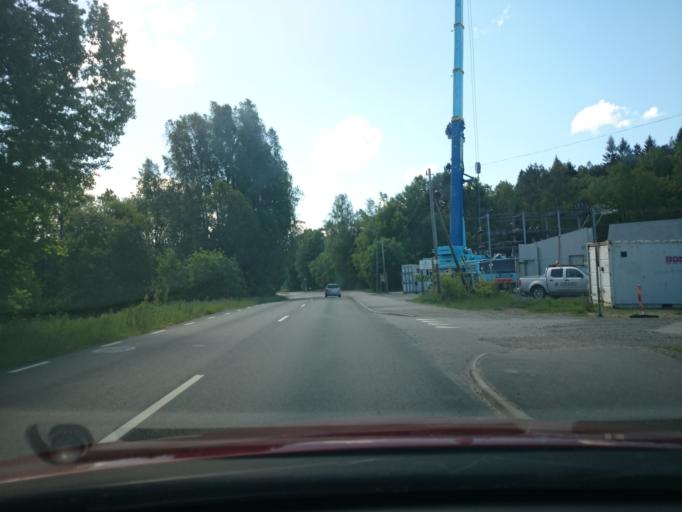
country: SE
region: Vaestra Goetaland
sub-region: Harryda Kommun
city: Landvetter
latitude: 57.6927
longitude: 12.2063
